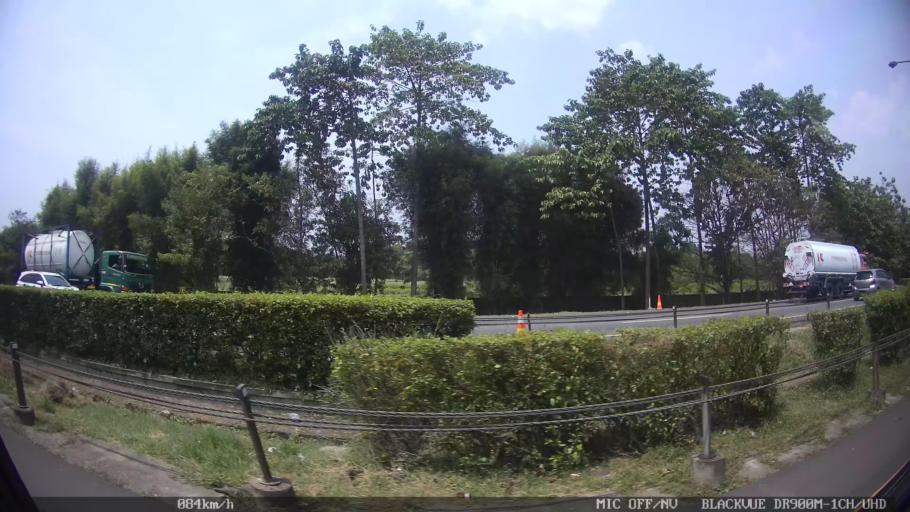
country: ID
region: Banten
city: Serang
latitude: -6.0841
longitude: 106.1357
